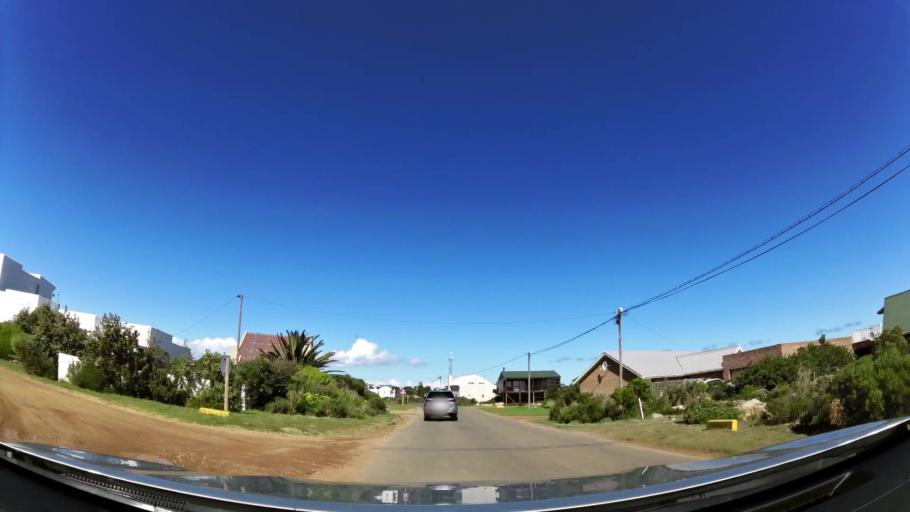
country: ZA
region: Western Cape
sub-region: Overberg District Municipality
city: Grabouw
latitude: -34.3690
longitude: 18.8914
